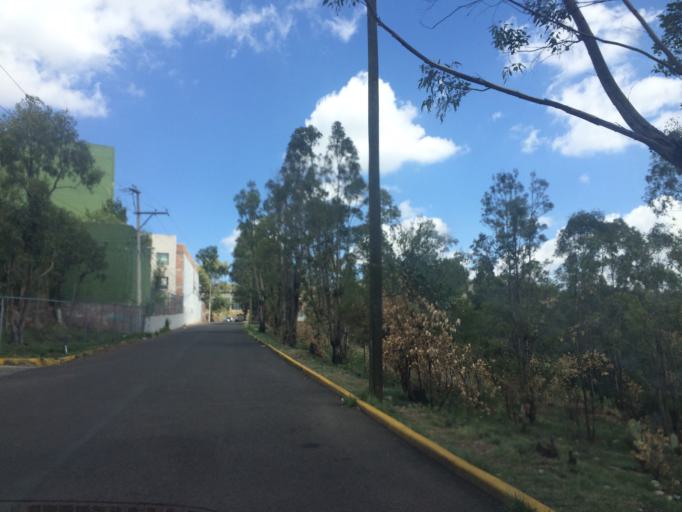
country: MX
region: Zacatecas
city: Zacatecas
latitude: 22.7576
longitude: -102.5797
